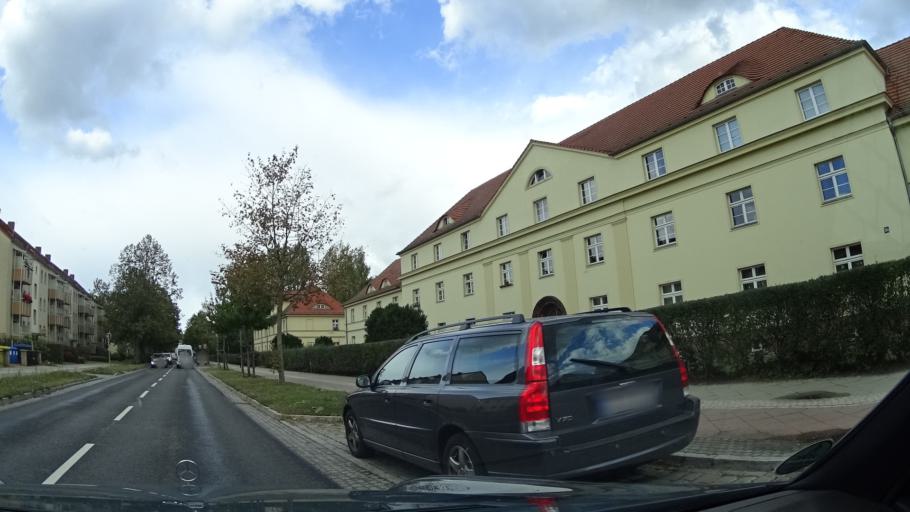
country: DE
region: Brandenburg
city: Neuruppin
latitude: 52.9104
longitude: 12.8014
